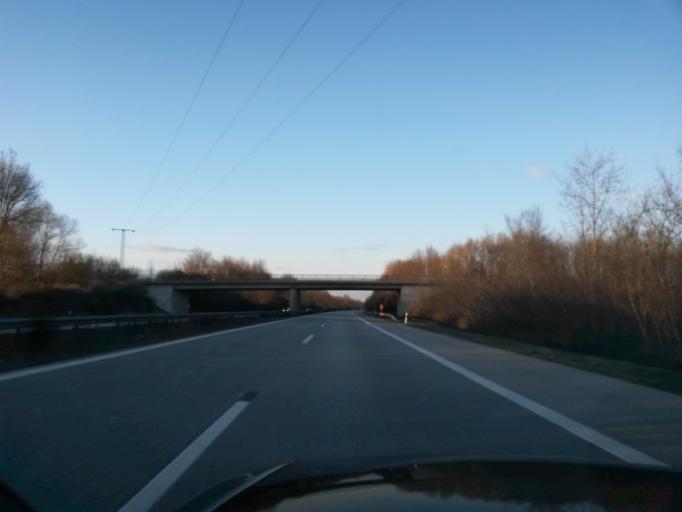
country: DE
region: Bavaria
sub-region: Upper Bavaria
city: Oberschleissheim
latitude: 48.2673
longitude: 11.5394
